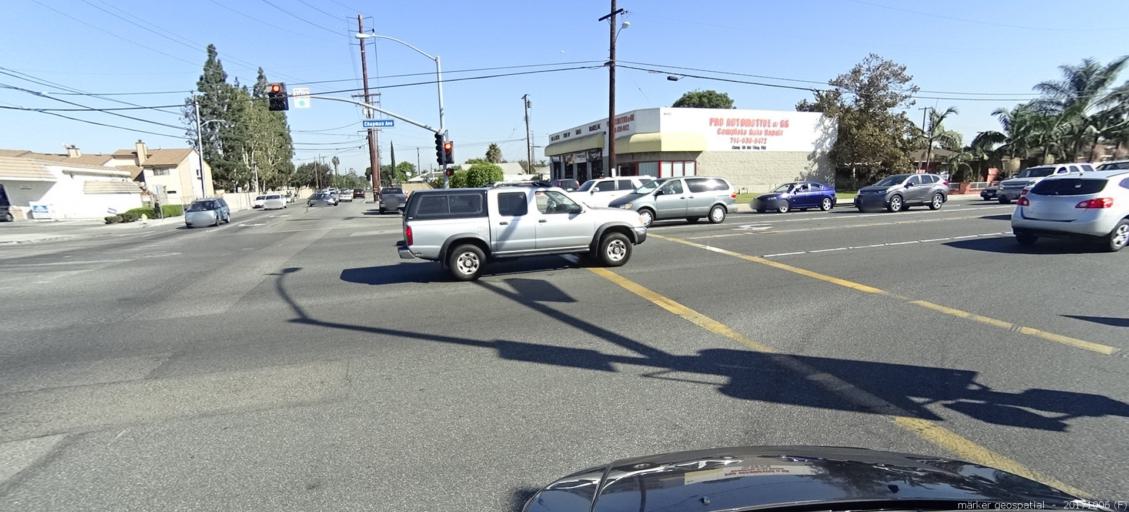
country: US
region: California
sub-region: Orange County
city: Stanton
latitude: 33.7883
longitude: -117.9841
